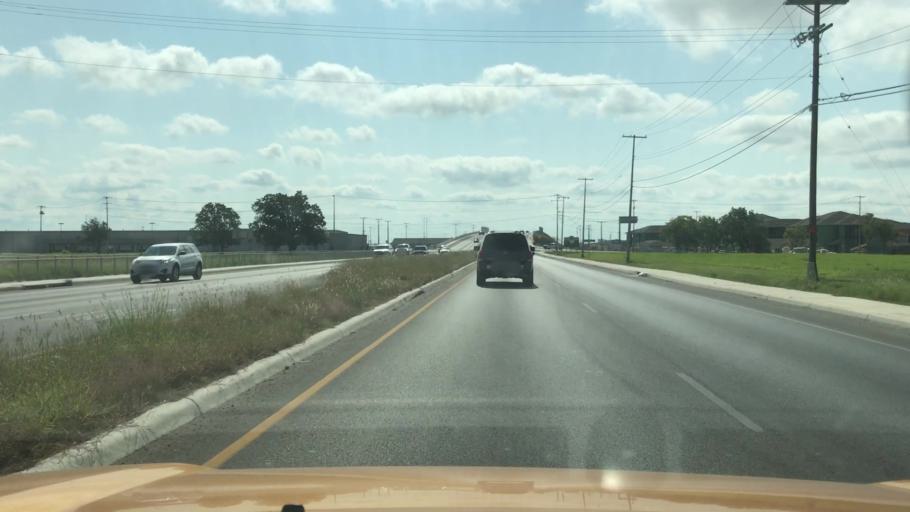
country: US
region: Texas
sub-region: Comal County
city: New Braunfels
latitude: 29.7404
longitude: -98.0924
